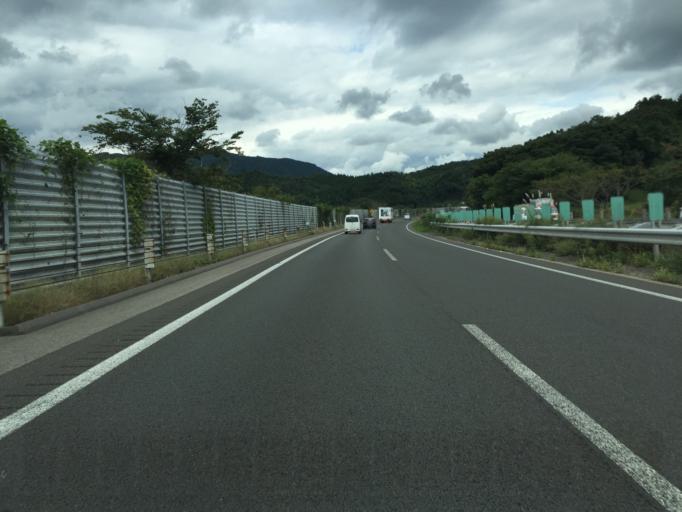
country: JP
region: Miyagi
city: Shiroishi
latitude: 37.9325
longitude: 140.6091
